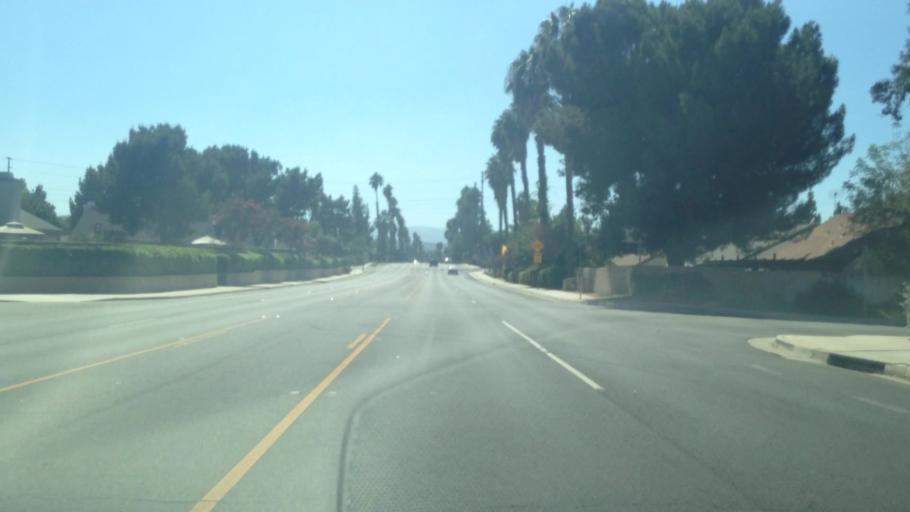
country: US
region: California
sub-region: Riverside County
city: Riverside
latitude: 33.9111
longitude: -117.4309
